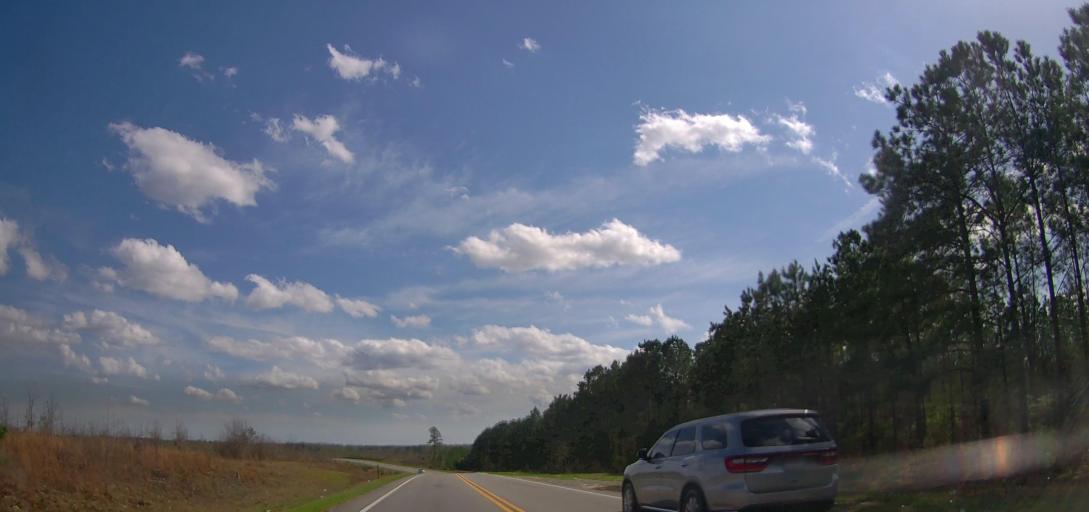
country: US
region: Georgia
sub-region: Wilkinson County
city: Gordon
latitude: 32.9444
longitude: -83.2898
